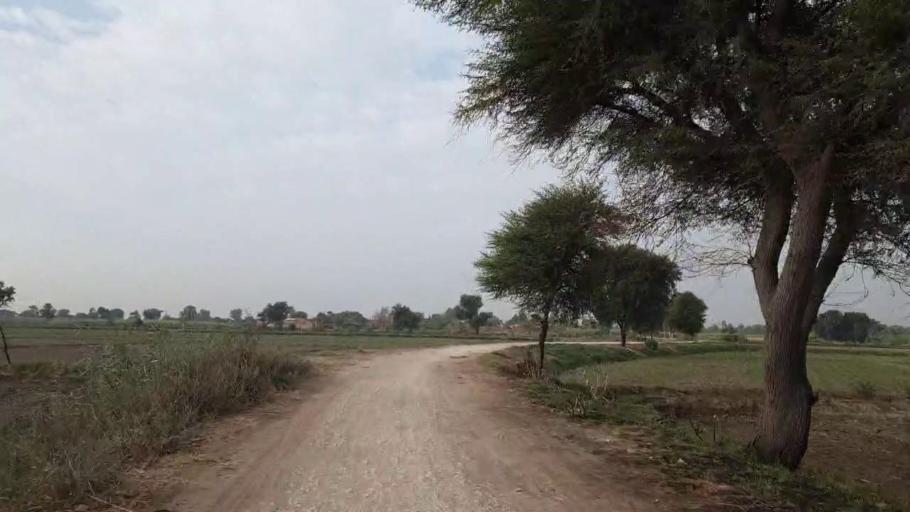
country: PK
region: Sindh
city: Tando Muhammad Khan
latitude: 25.0932
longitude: 68.4218
